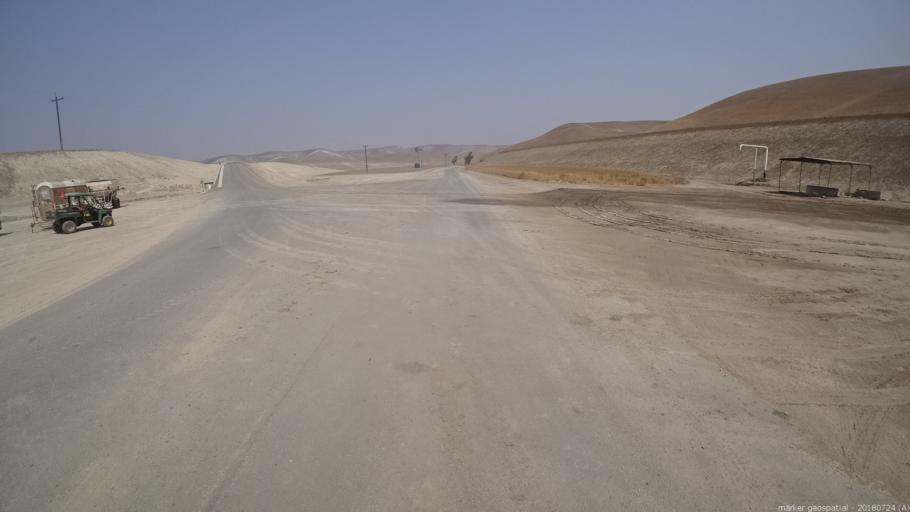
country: US
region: California
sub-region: Monterey County
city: King City
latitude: 36.1917
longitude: -121.0383
